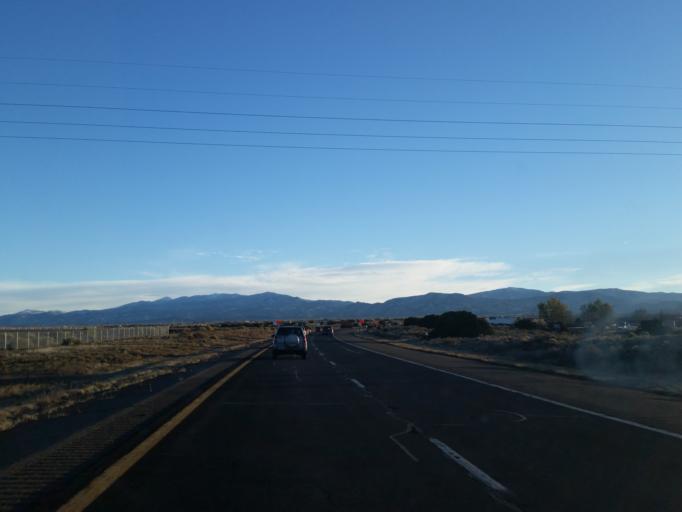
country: US
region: New Mexico
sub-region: Santa Fe County
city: Agua Fria
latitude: 35.6101
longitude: -106.0278
